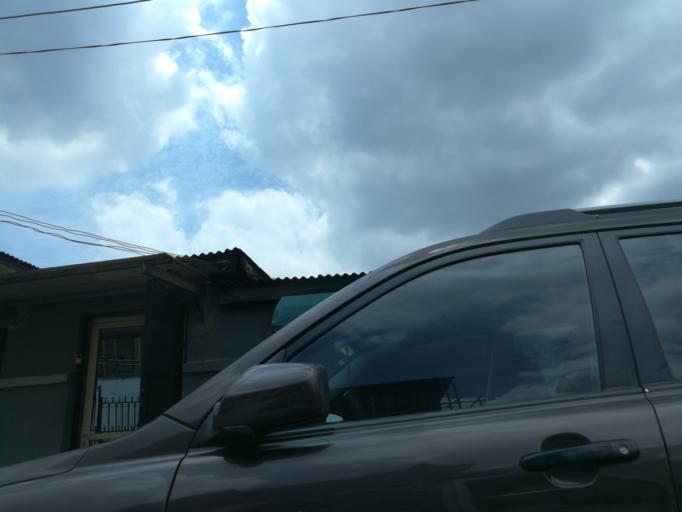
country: NG
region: Lagos
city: Ikeja
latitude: 6.6005
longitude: 3.3486
